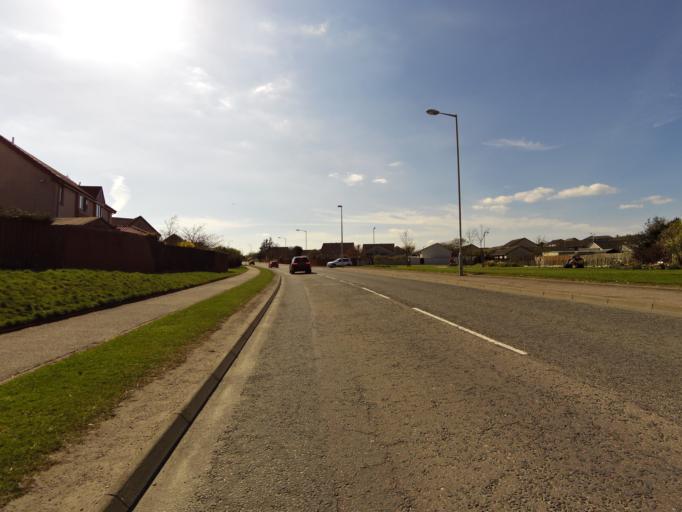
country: GB
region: Scotland
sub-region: Aberdeen City
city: Aberdeen
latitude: 57.0982
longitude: -2.0857
